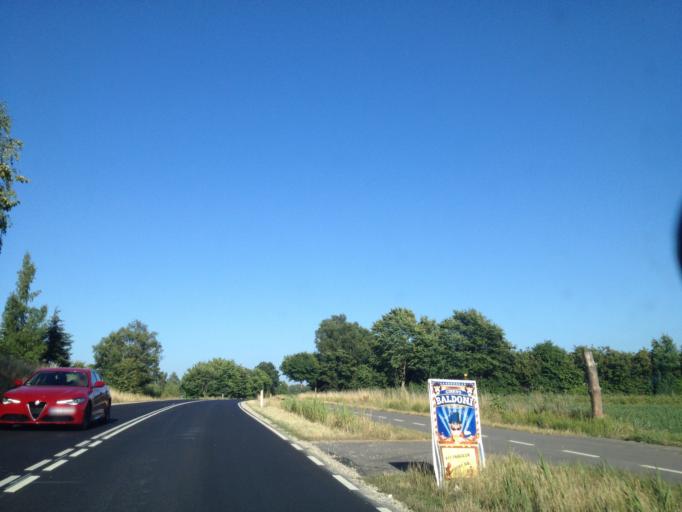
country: DK
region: Capital Region
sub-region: Halsnaes Kommune
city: Frederiksvaerk
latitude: 56.0191
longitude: 12.0916
